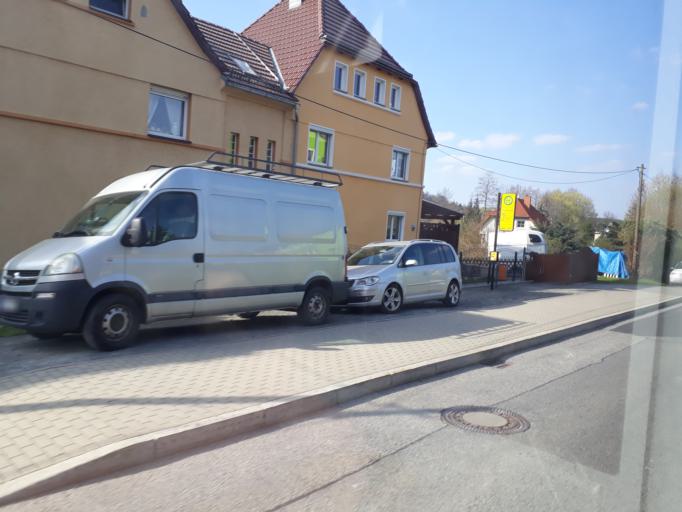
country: DE
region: Saxony
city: Kreischa
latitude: 50.9507
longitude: 13.7690
